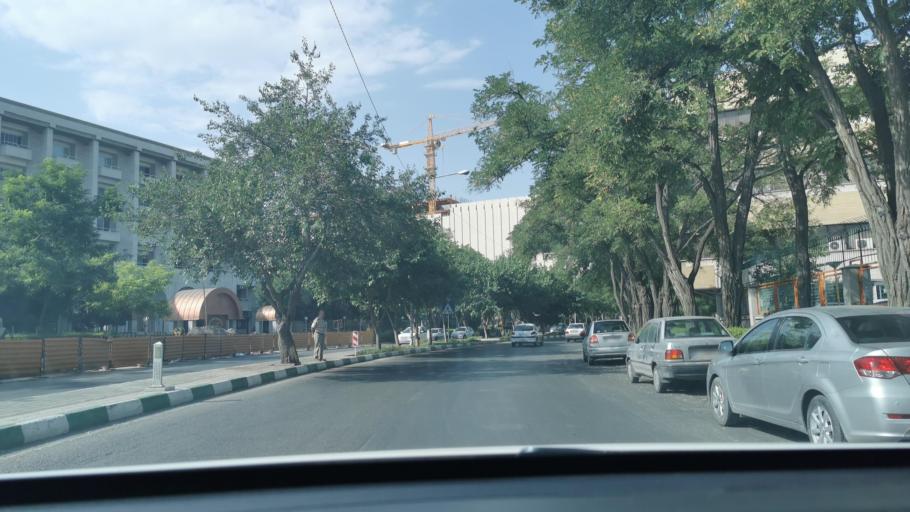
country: IR
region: Razavi Khorasan
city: Mashhad
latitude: 36.3208
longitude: 59.5630
